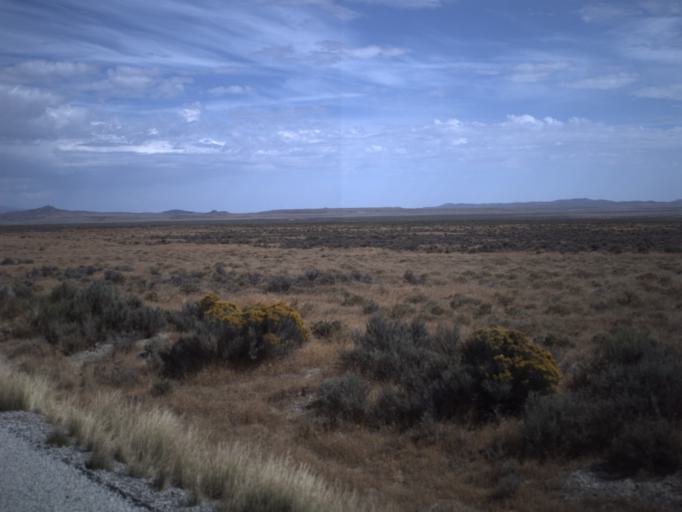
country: US
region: Utah
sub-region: Tooele County
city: Wendover
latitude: 41.5439
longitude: -113.5891
